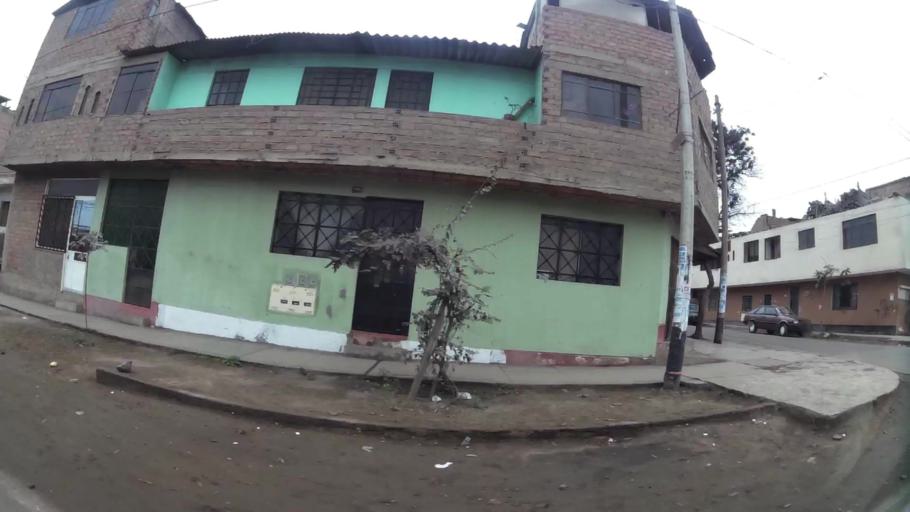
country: PE
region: Lima
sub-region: Lima
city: Surco
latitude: -12.1753
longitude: -76.9454
